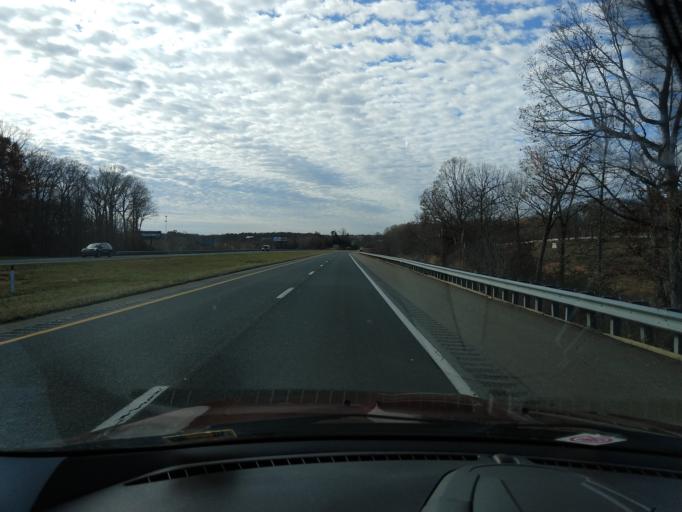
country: US
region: Virginia
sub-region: Campbell County
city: Timberlake
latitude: 37.3229
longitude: -79.2170
